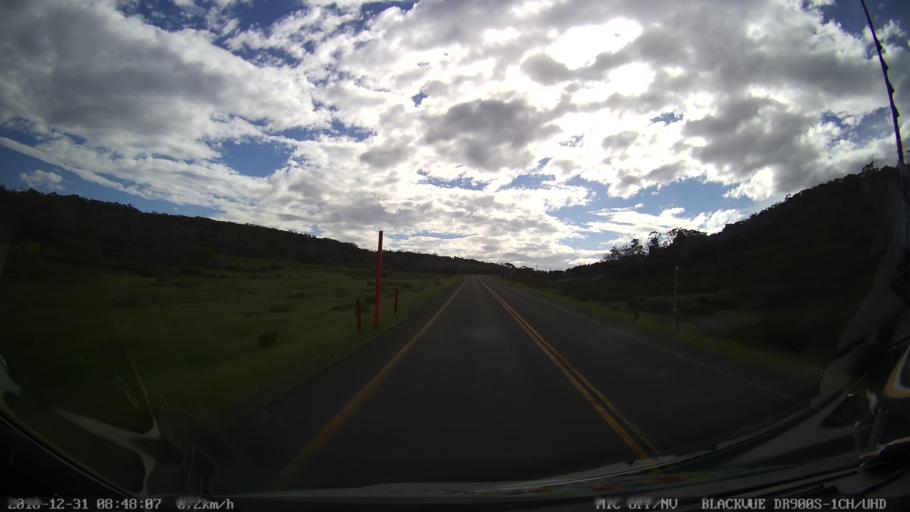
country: AU
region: New South Wales
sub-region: Snowy River
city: Jindabyne
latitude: -36.3591
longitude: 148.4925
